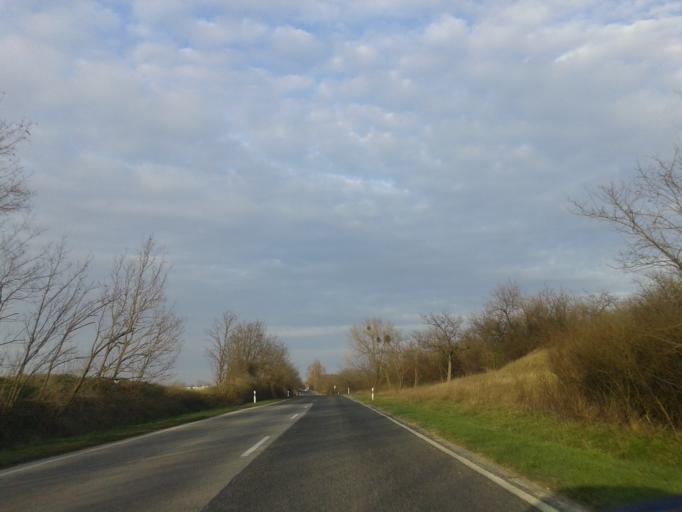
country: HU
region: Komarom-Esztergom
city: Komarom
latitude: 47.7348
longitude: 18.0689
